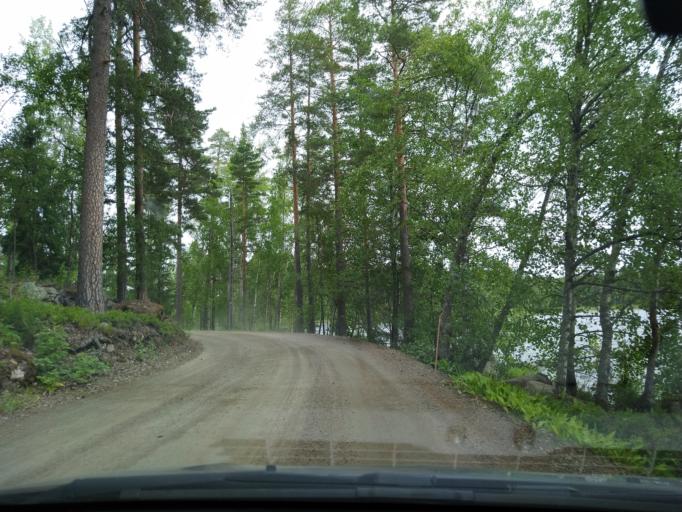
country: FI
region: Southern Savonia
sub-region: Mikkeli
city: Maentyharju
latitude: 61.1367
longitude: 26.8874
